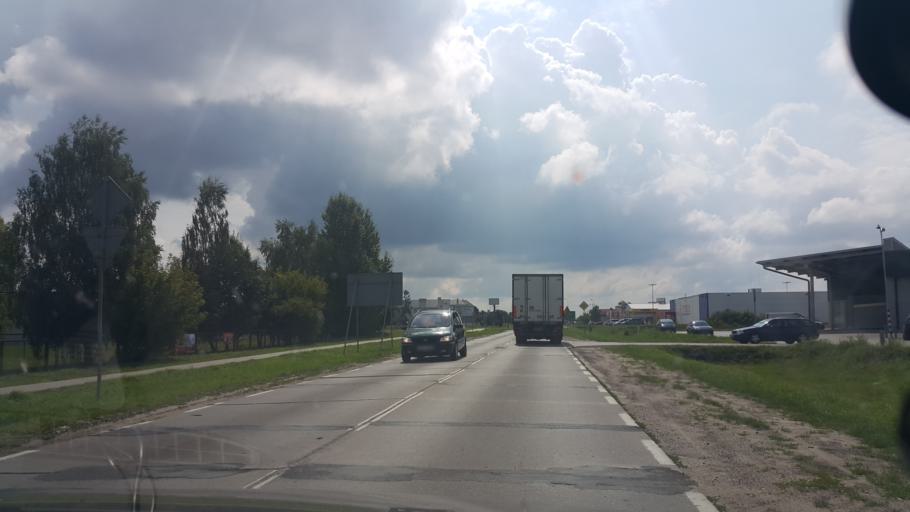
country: PL
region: Lublin Voivodeship
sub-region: Powiat wlodawski
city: Wlodawa
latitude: 51.5490
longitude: 23.5401
